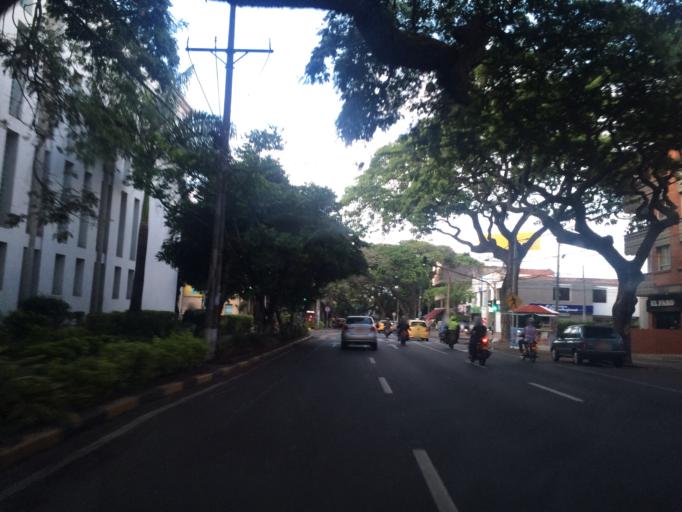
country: CO
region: Valle del Cauca
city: Cali
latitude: 3.4710
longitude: -76.5274
